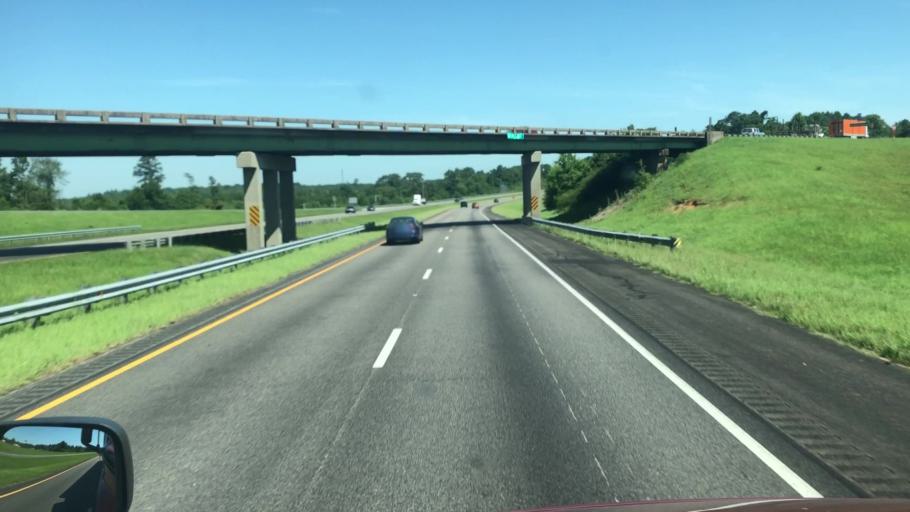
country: US
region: Alabama
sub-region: Autauga County
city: Pine Level
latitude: 32.5494
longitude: -86.4573
